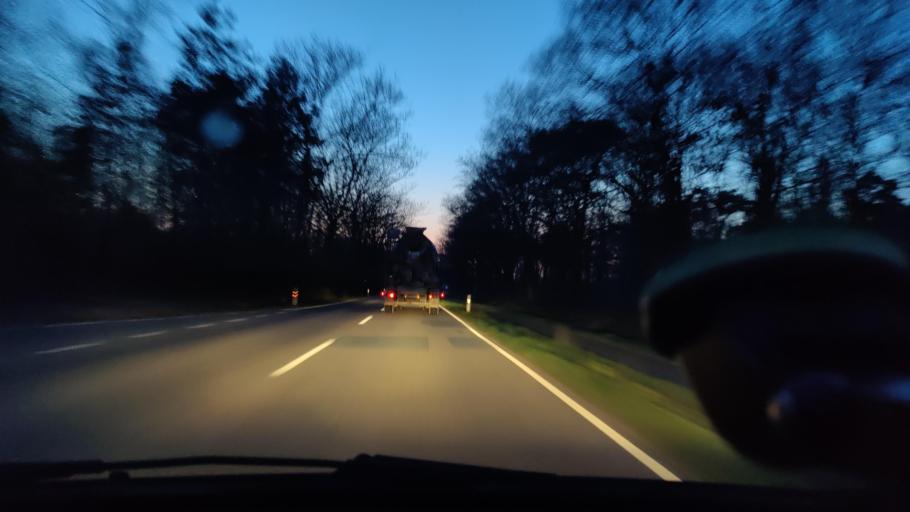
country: DE
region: North Rhine-Westphalia
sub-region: Regierungsbezirk Dusseldorf
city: Sonsbeck
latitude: 51.5889
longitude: 6.4152
